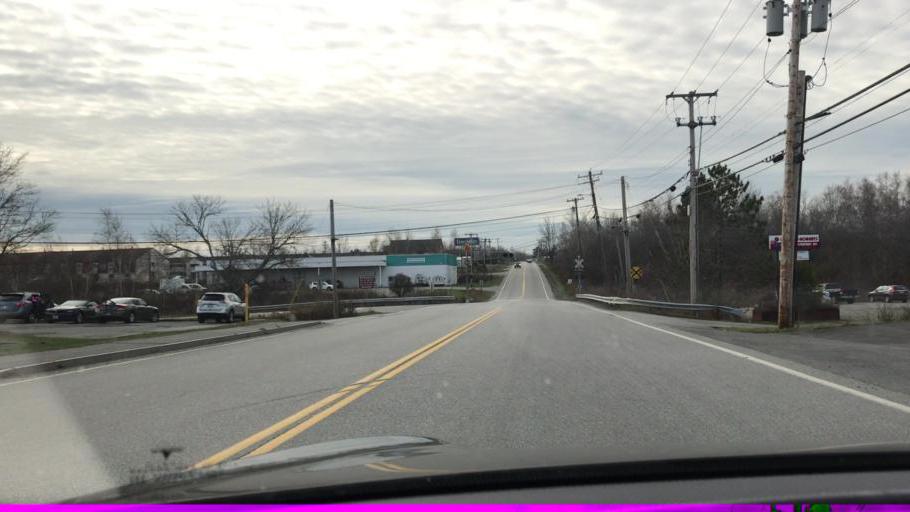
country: US
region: Maine
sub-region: Penobscot County
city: Bangor
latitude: 44.7861
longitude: -68.8137
